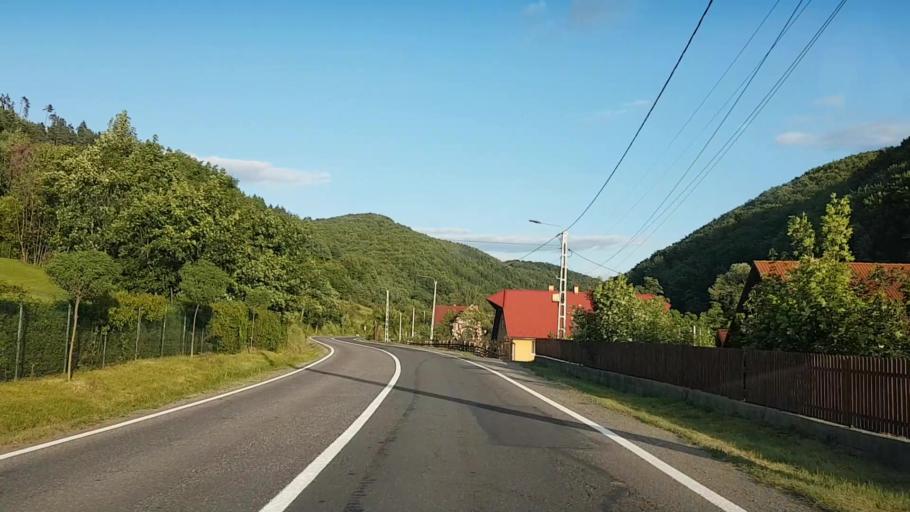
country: RO
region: Harghita
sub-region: Comuna Corund
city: Corund
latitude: 46.4671
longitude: 25.2025
